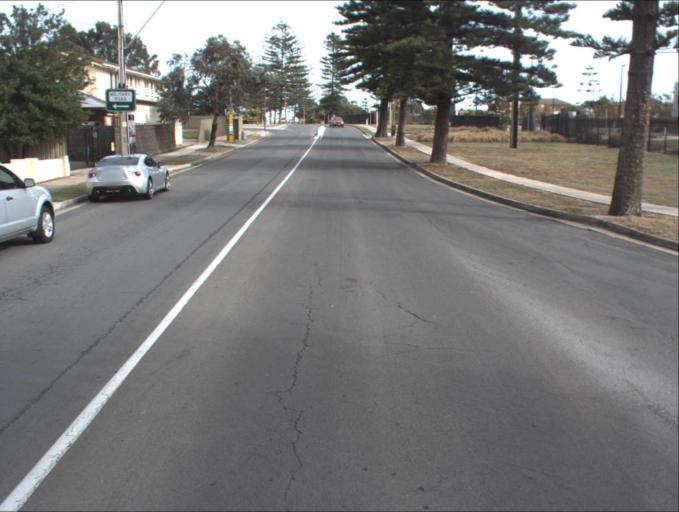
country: AU
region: South Australia
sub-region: Port Adelaide Enfield
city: Birkenhead
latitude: -34.8121
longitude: 138.4960
